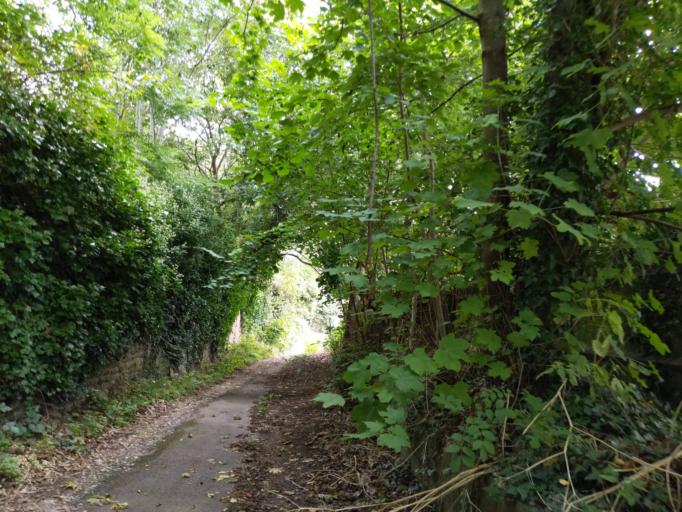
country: GB
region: England
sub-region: Oxfordshire
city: Radley
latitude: 51.7168
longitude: -1.2430
